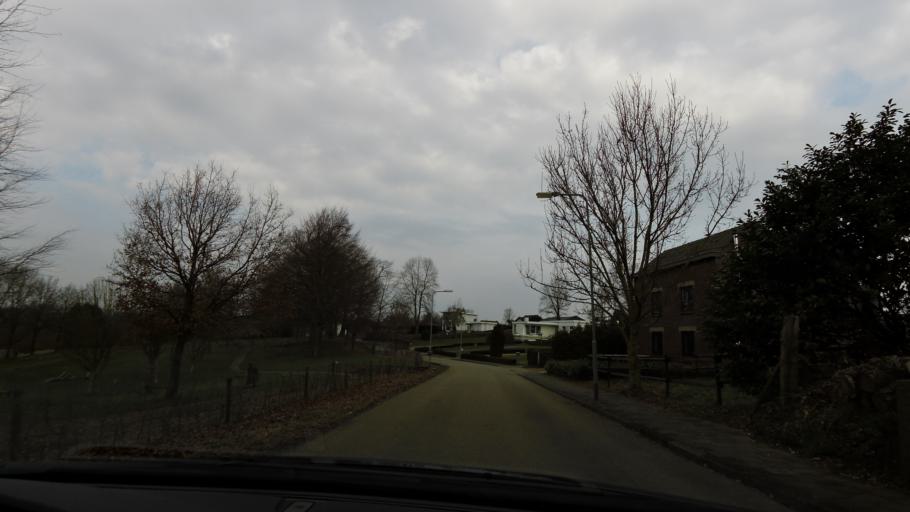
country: NL
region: Limburg
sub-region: Gemeente Simpelveld
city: Simpelveld
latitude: 50.8236
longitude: 6.0052
